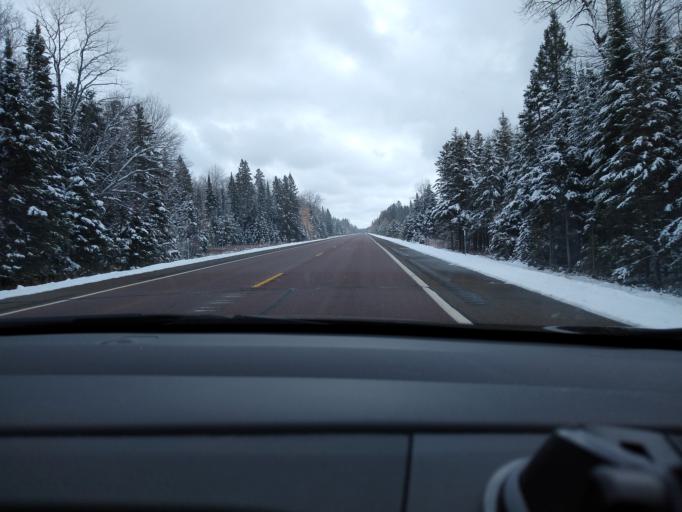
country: US
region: Michigan
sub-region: Iron County
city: Iron River
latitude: 46.1695
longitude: -88.9298
